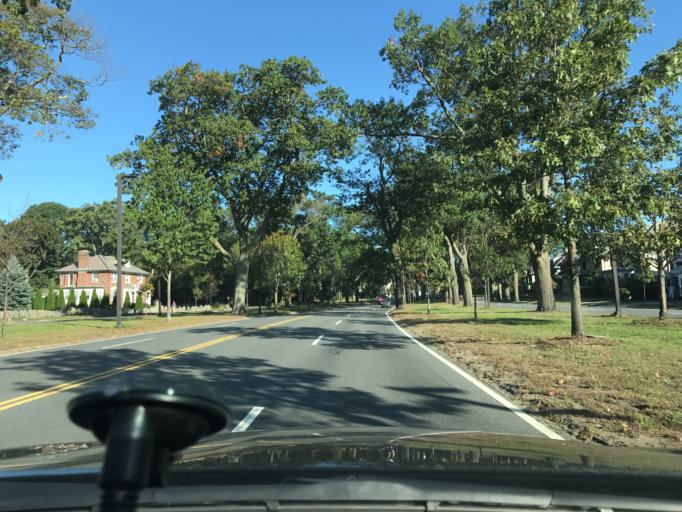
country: US
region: Massachusetts
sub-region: Suffolk County
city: Jamaica Plain
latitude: 42.3100
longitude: -71.1220
